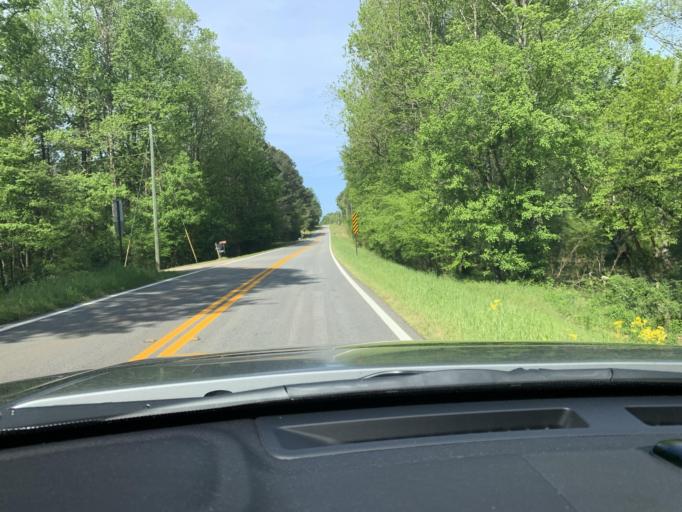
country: US
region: Georgia
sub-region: Oconee County
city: Watkinsville
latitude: 33.8165
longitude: -83.3795
